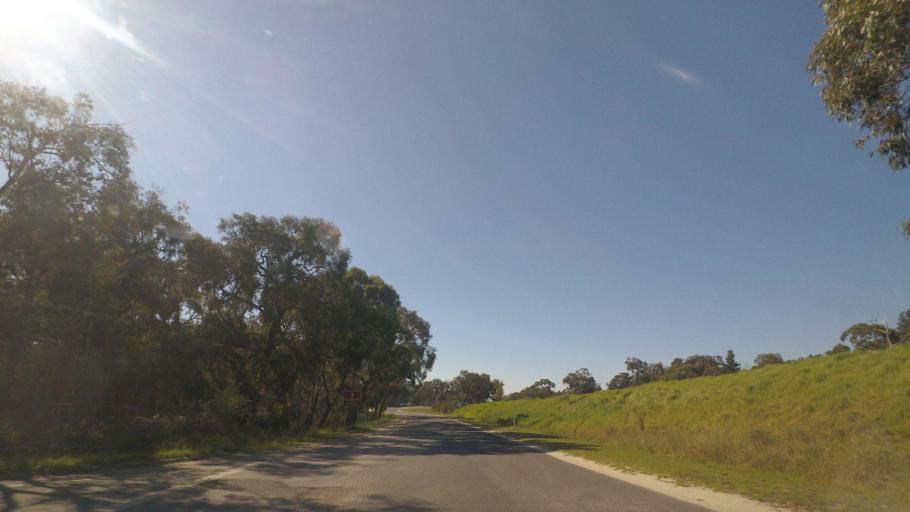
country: AU
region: Victoria
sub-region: Cardinia
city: Garfield
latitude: -38.0716
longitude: 145.6539
